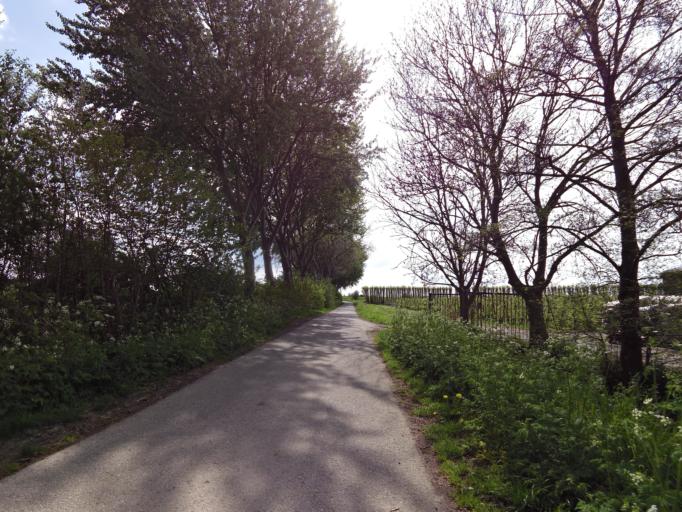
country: NL
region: South Holland
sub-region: Gemeente Brielle
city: Brielle
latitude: 51.8995
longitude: 4.1872
